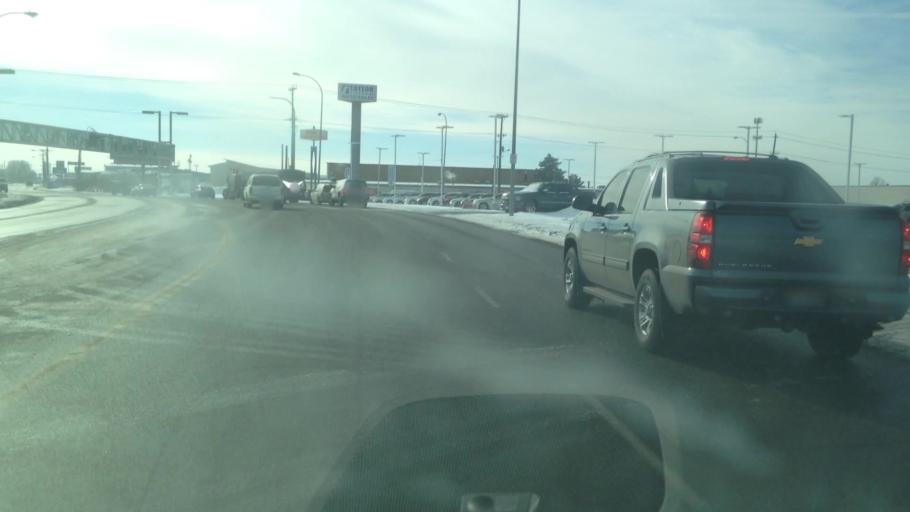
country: US
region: Idaho
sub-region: Bonneville County
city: Idaho Falls
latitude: 43.5126
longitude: -112.0239
